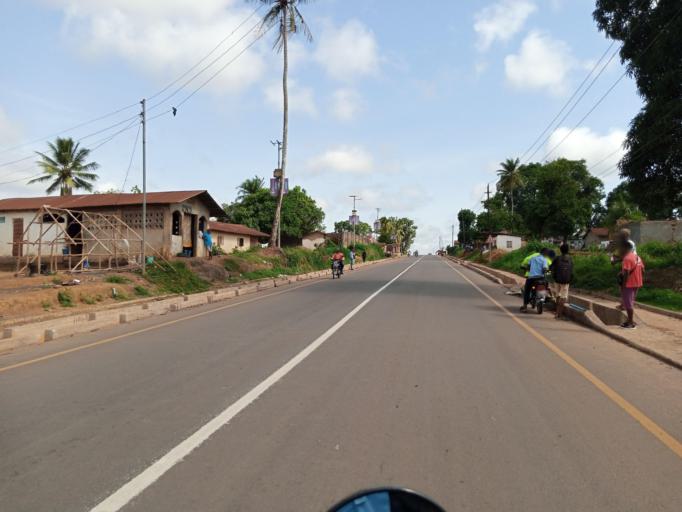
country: SL
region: Southern Province
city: Bo
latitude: 7.9523
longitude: -11.7181
